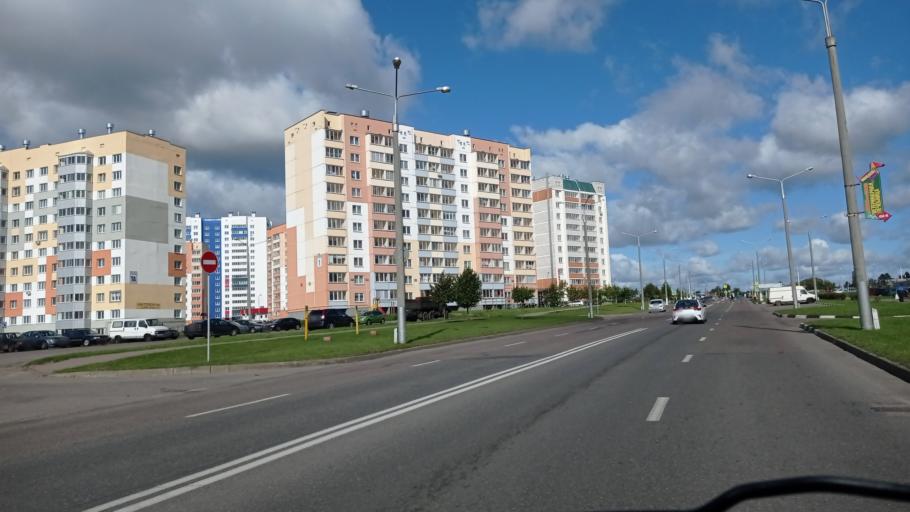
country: BY
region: Vitebsk
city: Vitebsk
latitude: 55.1712
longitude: 30.2575
